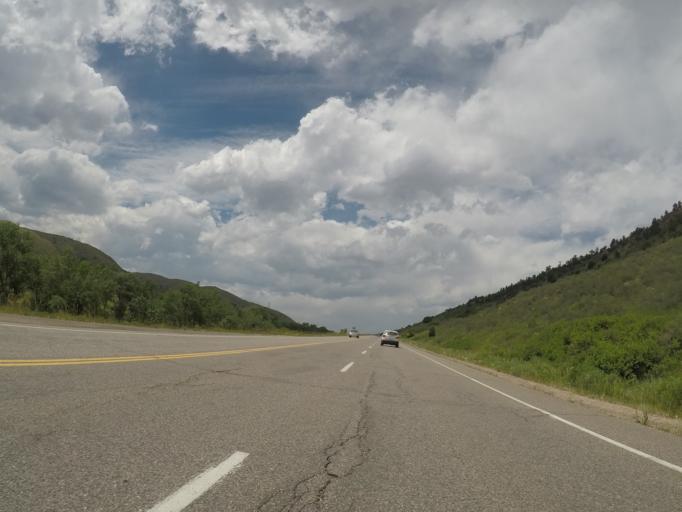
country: US
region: Colorado
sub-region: Jefferson County
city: West Pleasant View
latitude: 39.6849
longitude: -105.1993
